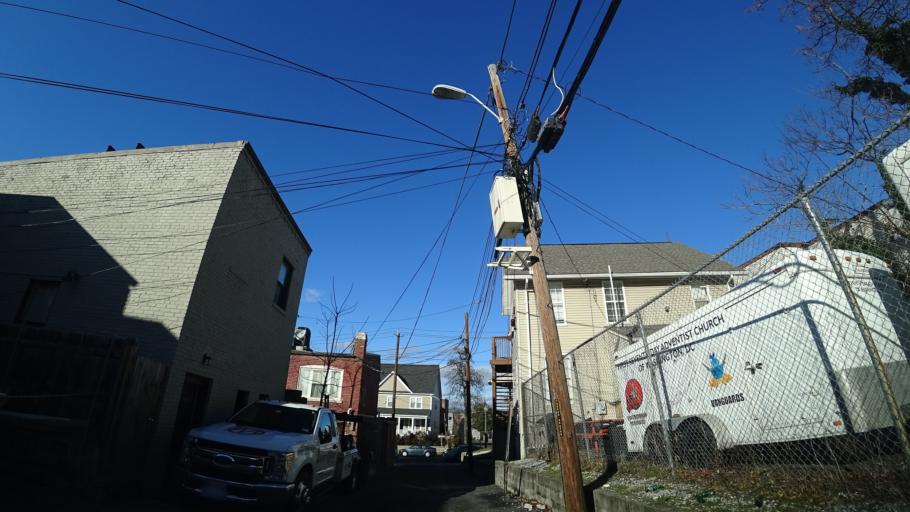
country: US
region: Maryland
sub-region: Prince George's County
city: Chillum
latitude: 38.9394
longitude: -77.0243
